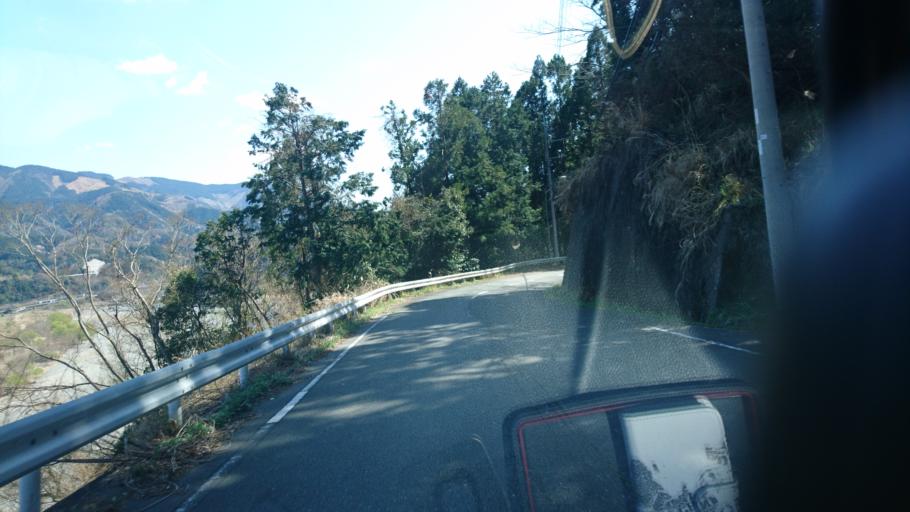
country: JP
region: Shizuoka
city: Fujinomiya
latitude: 35.3494
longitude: 138.4377
